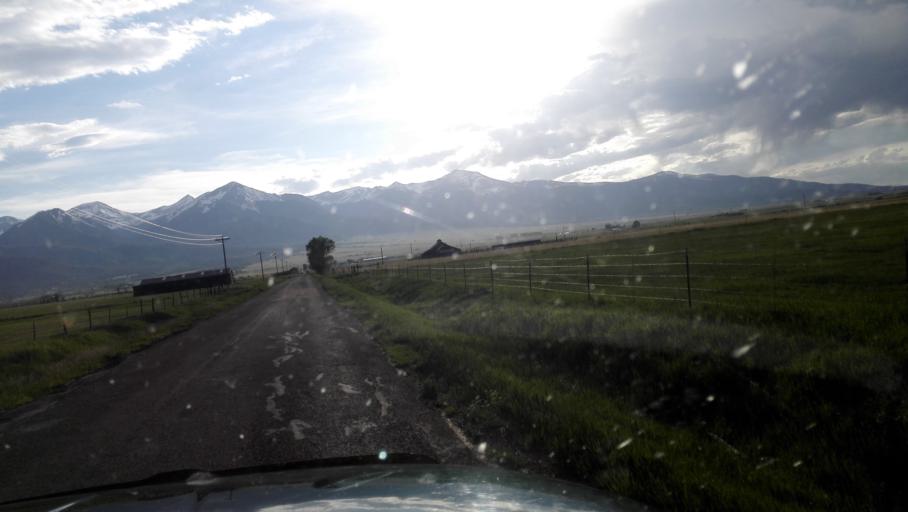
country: US
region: Colorado
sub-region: Custer County
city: Westcliffe
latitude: 38.1317
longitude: -105.4944
